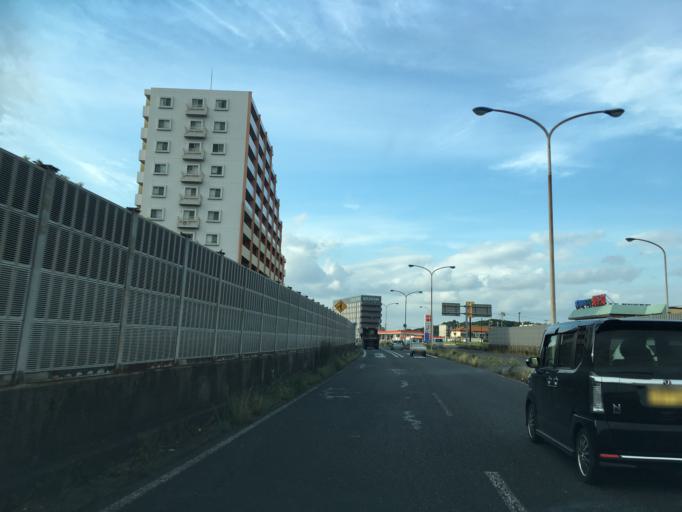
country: JP
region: Chiba
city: Kisarazu
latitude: 35.3788
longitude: 139.9421
